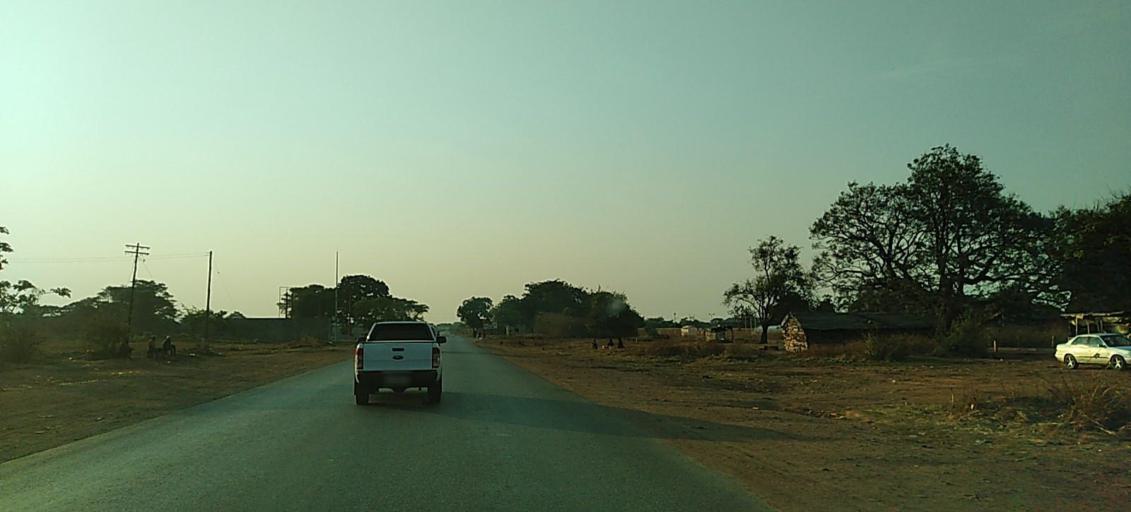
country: ZM
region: Copperbelt
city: Ndola
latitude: -13.0378
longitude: 28.6917
